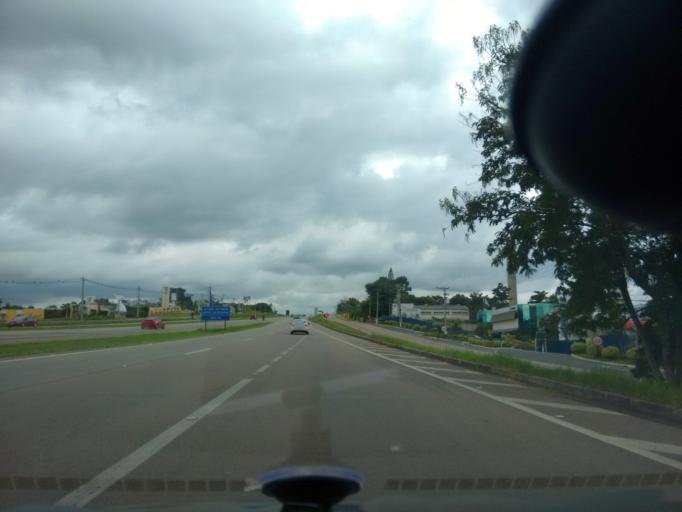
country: BR
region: Sao Paulo
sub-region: Indaiatuba
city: Indaiatuba
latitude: -23.0850
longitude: -47.1768
